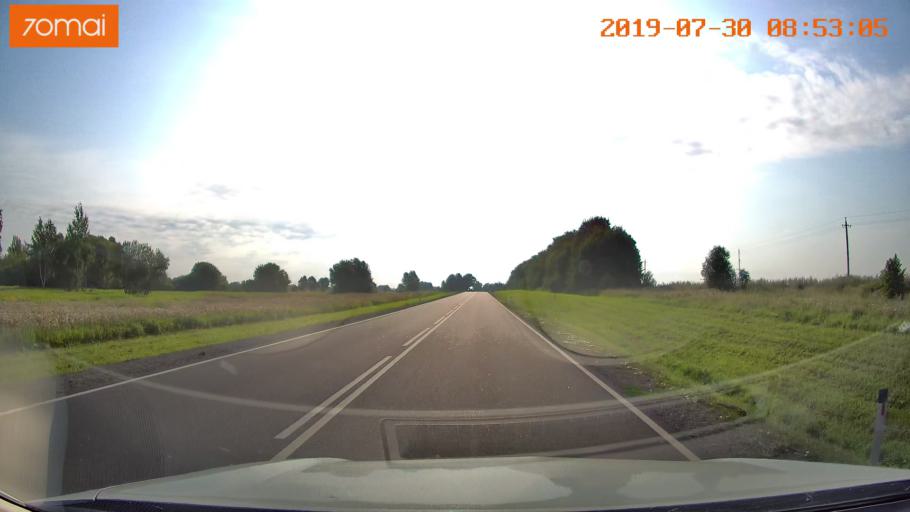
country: RU
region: Kaliningrad
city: Chernyakhovsk
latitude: 54.6021
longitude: 21.9885
